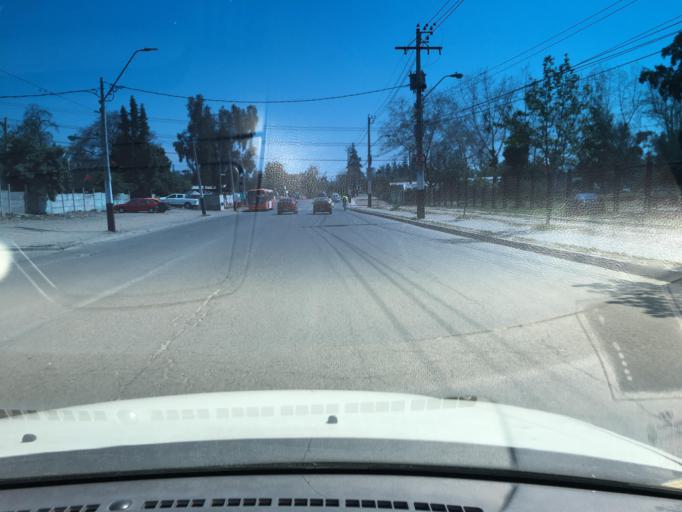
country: CL
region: Santiago Metropolitan
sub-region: Provincia de Santiago
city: Villa Presidente Frei, Nunoa, Santiago, Chile
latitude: -33.5177
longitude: -70.5564
